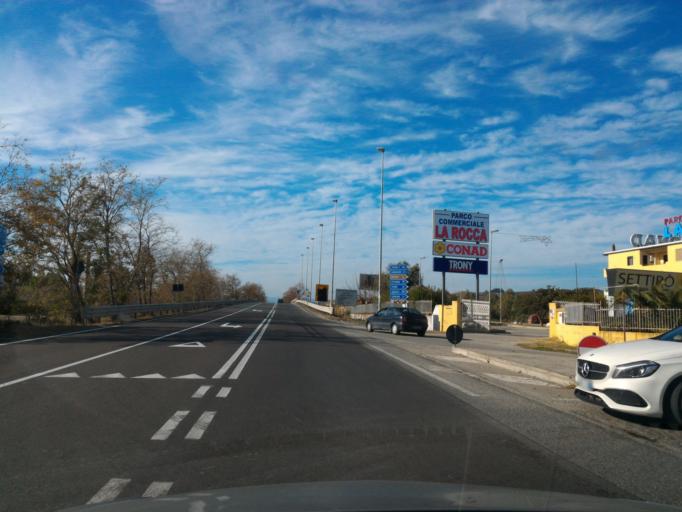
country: IT
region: Calabria
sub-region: Provincia di Catanzaro
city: Cropani Marina
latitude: 38.9198
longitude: 16.7975
